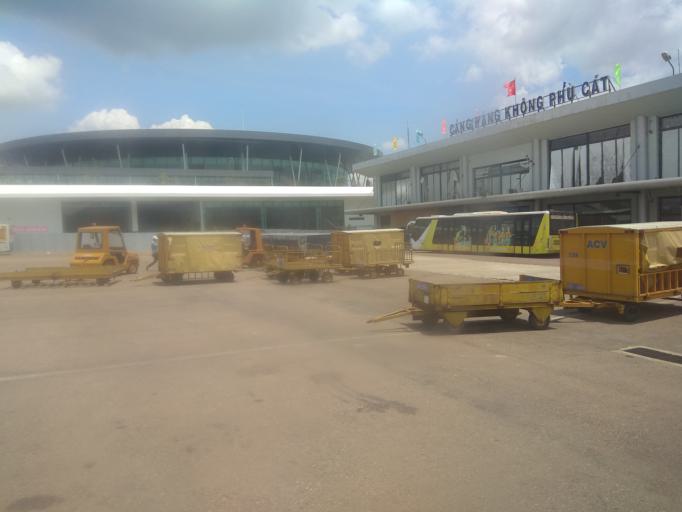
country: VN
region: Binh Dinh
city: Phu Cat
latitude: 13.9526
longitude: 109.0490
